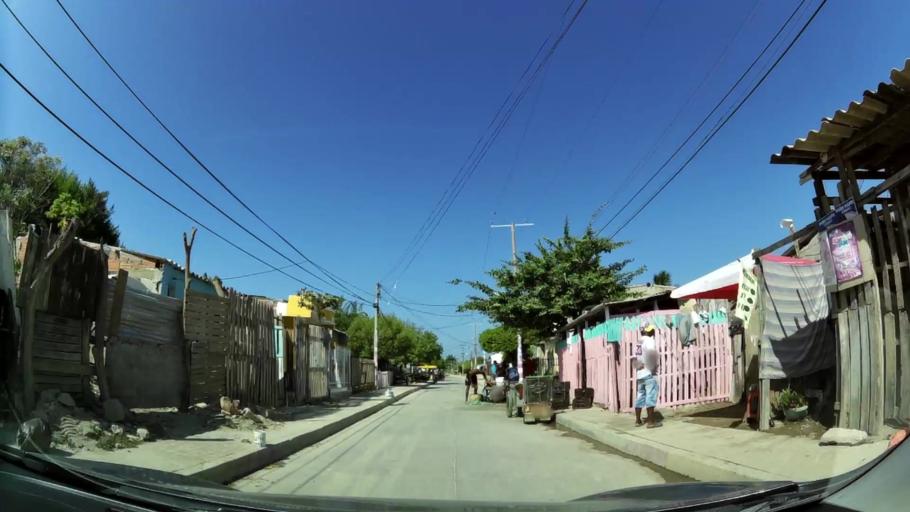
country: CO
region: Bolivar
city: Cartagena
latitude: 10.4124
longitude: -75.5134
